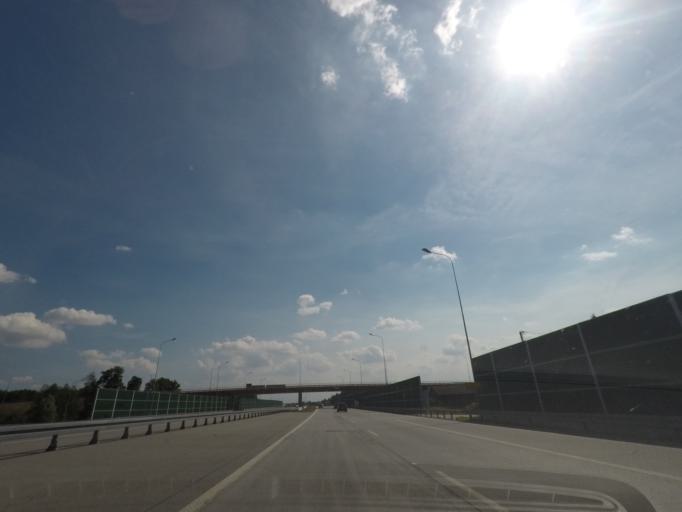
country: PL
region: Lodz Voivodeship
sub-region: Powiat lodzki wschodni
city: Tuszyn
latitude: 51.6328
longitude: 19.5691
